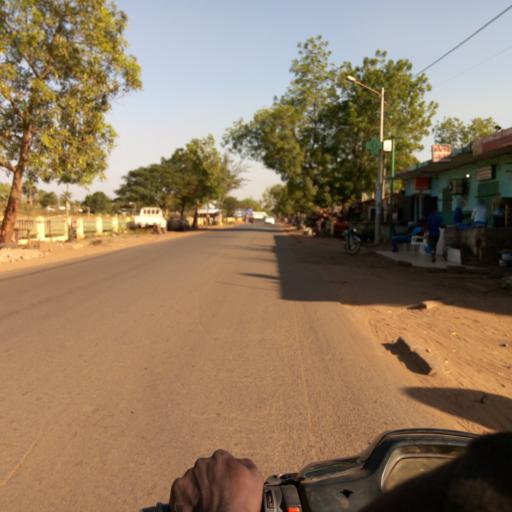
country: ML
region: Bamako
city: Bamako
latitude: 12.6521
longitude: -8.0161
